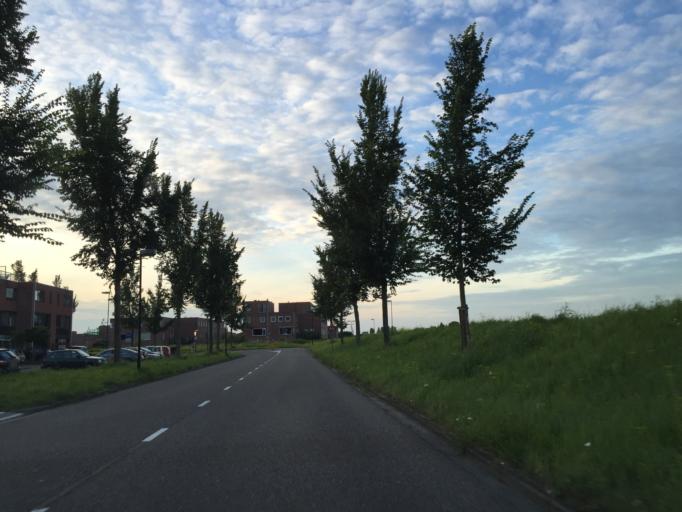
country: NL
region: South Holland
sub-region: Gemeente Rijnwoude
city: Benthuizen
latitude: 52.0767
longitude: 4.5293
